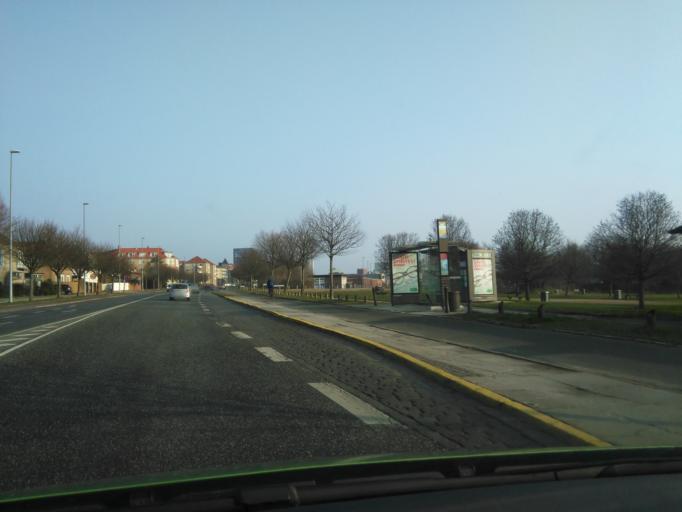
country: DK
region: Central Jutland
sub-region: Arhus Kommune
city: Arhus
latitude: 56.1393
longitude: 10.2070
